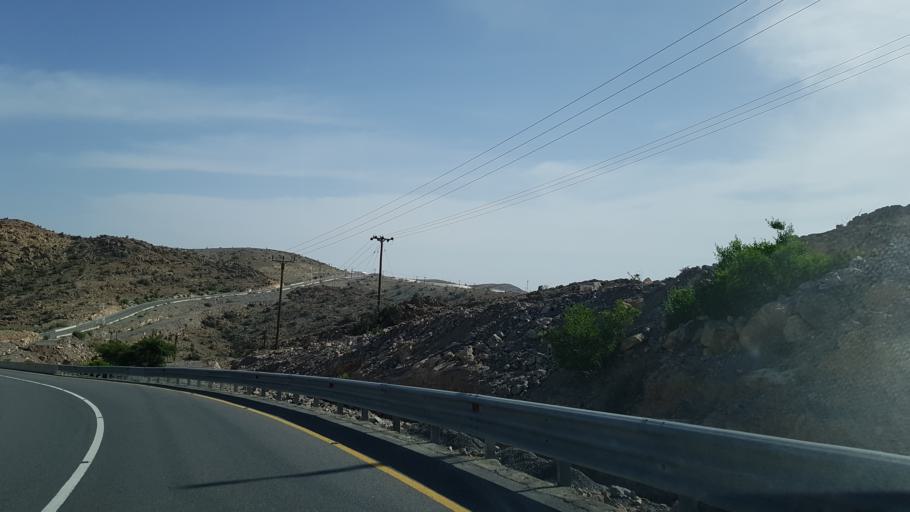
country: OM
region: Muhafazat ad Dakhiliyah
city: Izki
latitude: 23.0372
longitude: 57.7046
